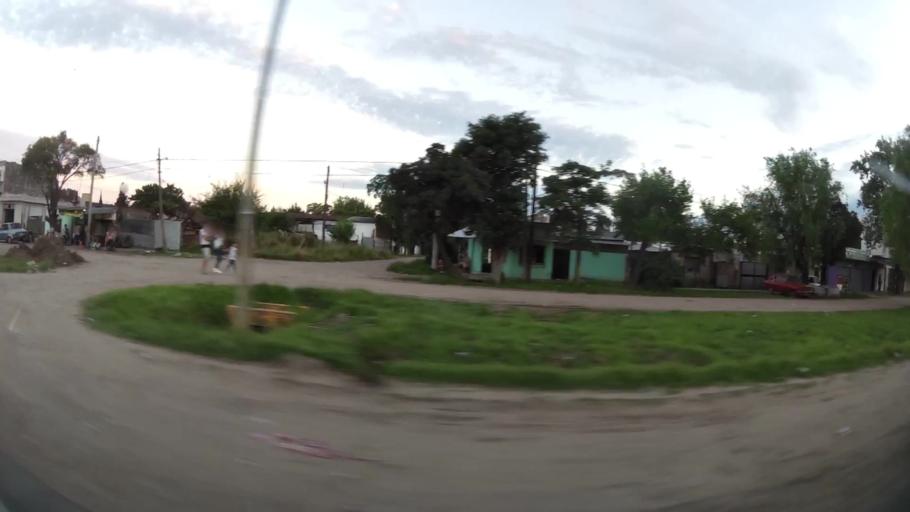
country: AR
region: Buenos Aires
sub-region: Partido de Merlo
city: Merlo
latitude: -34.6896
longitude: -58.7669
